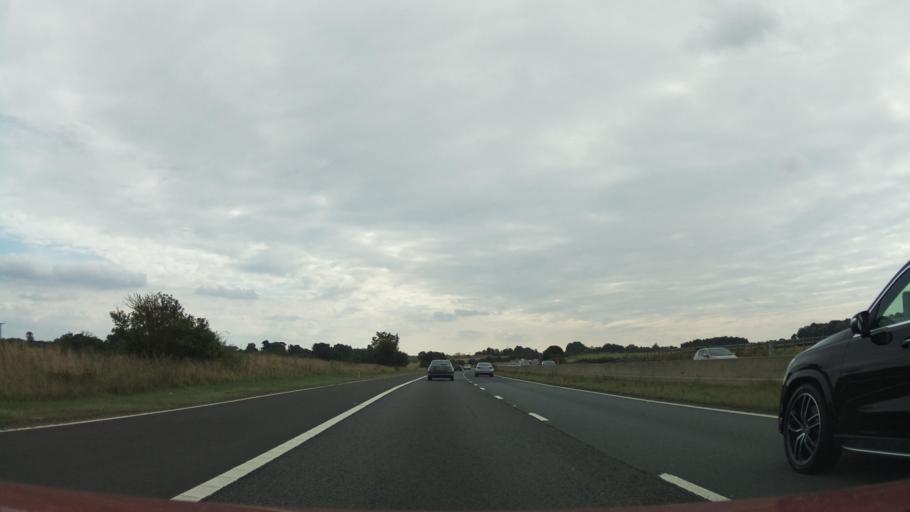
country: GB
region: England
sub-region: County Durham
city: West Rainton
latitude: 54.8428
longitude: -1.5255
